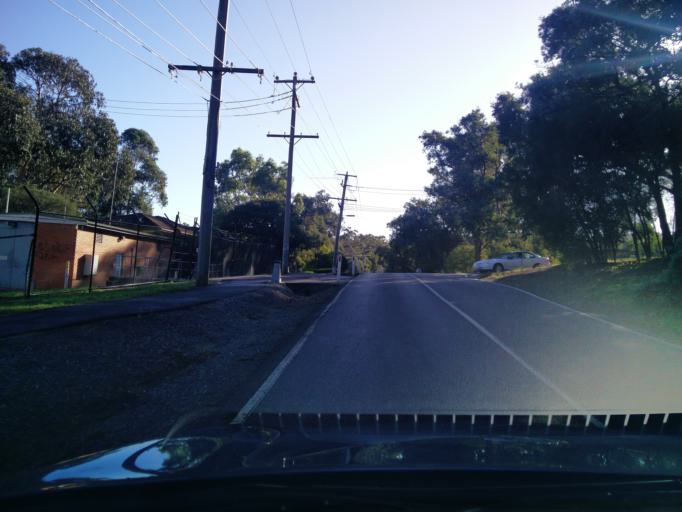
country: AU
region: Victoria
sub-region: Nillumbik
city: Research
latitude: -37.7050
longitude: 145.1759
